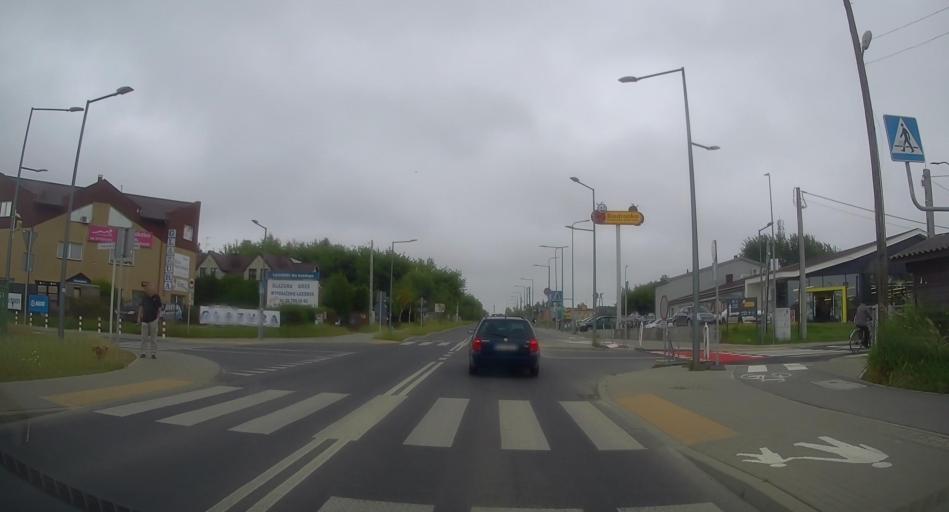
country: PL
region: Masovian Voivodeship
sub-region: Powiat piaseczynski
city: Piaseczno
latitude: 52.0723
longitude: 21.0160
